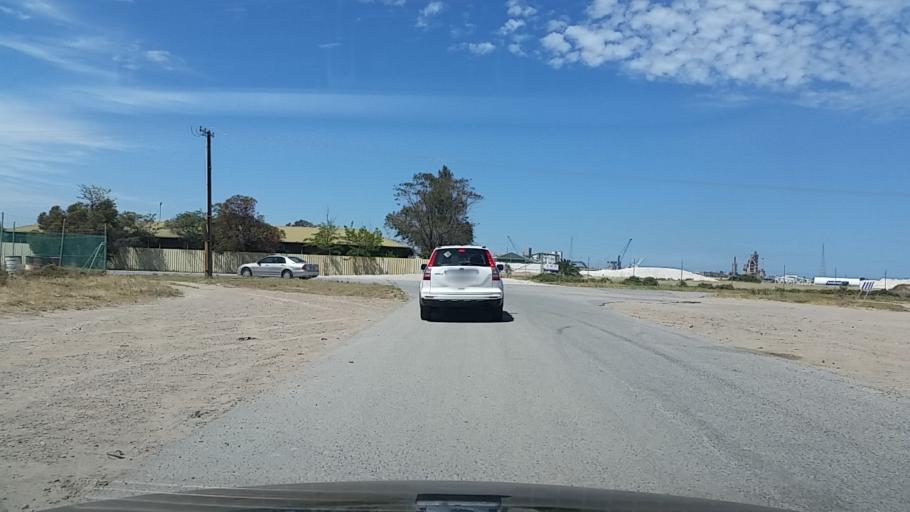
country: AU
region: South Australia
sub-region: Port Adelaide Enfield
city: Birkenhead
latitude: -34.8124
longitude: 138.5189
